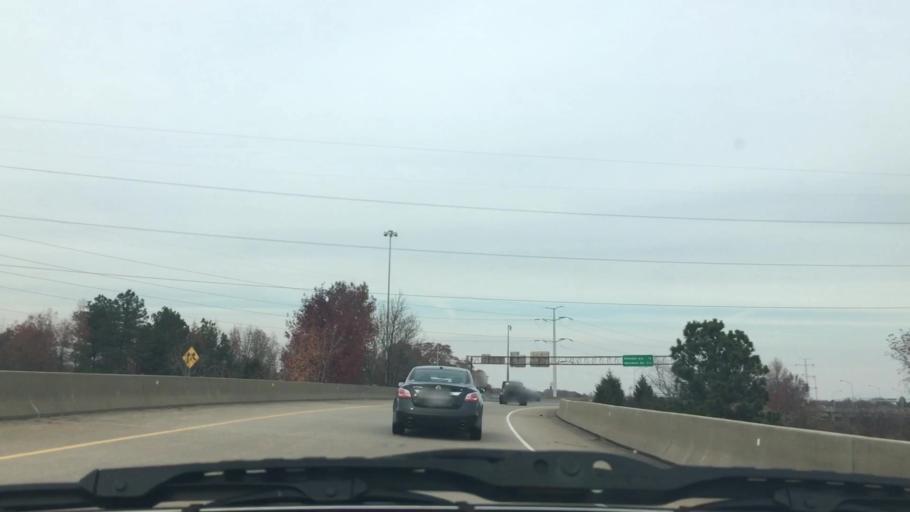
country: US
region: Virginia
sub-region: City of Newport News
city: Newport News
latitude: 36.9893
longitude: -76.4254
